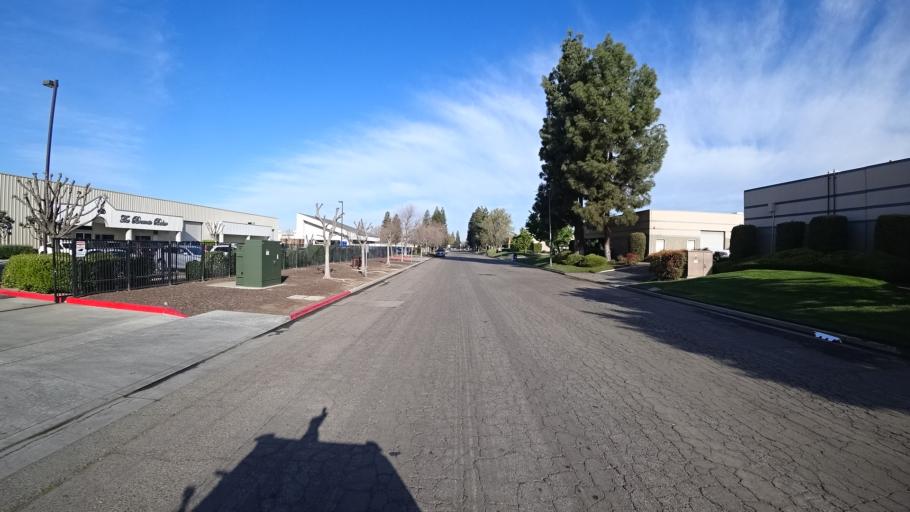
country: US
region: California
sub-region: Fresno County
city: West Park
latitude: 36.8107
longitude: -119.8772
